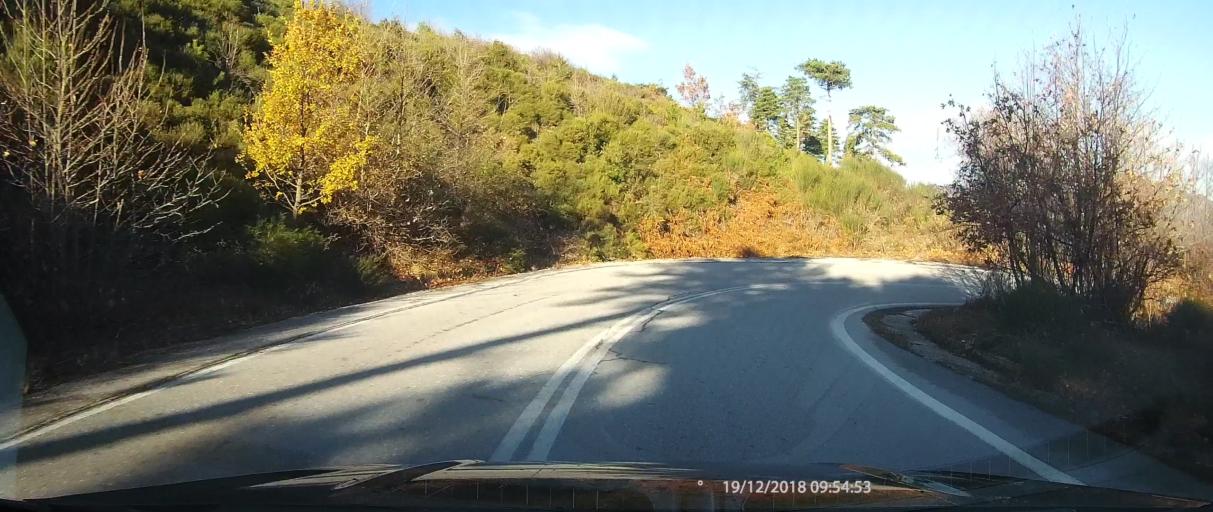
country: GR
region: Peloponnese
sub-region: Nomos Messinias
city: Paralia Vergas
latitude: 37.0829
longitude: 22.2425
